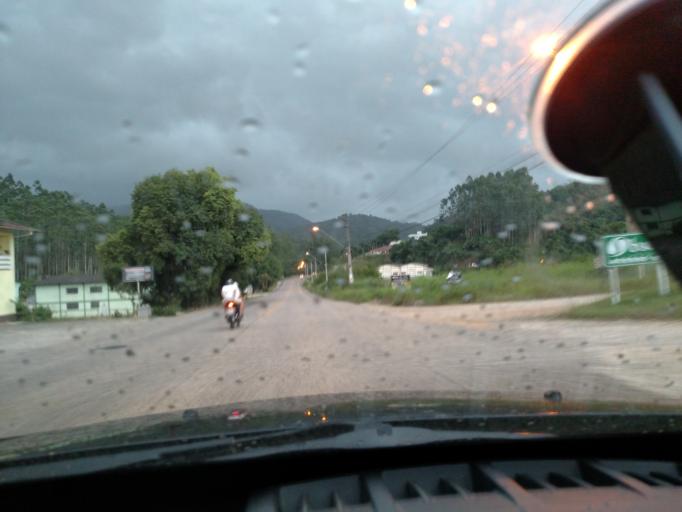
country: BR
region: Santa Catarina
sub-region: Brusque
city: Brusque
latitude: -27.0554
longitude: -48.8916
